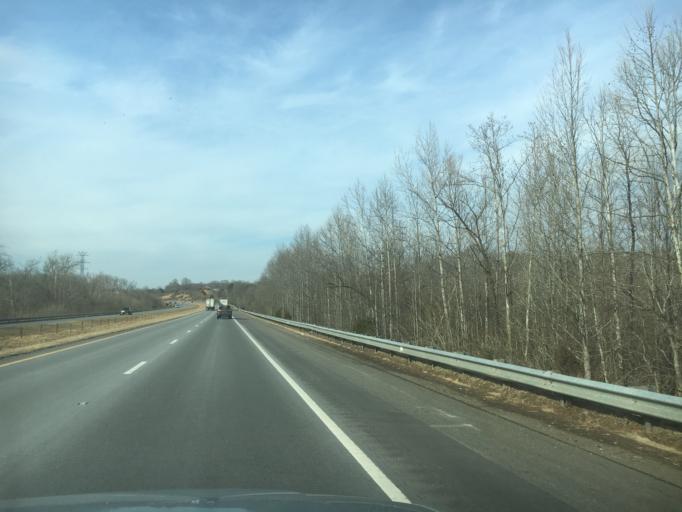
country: US
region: North Carolina
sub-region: Catawba County
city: Maiden
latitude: 35.6059
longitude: -81.2726
